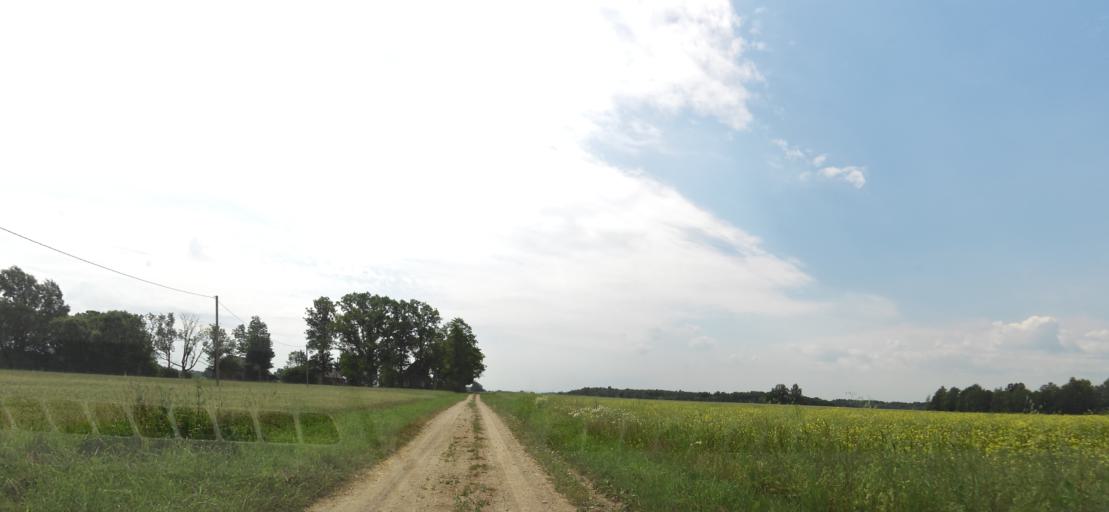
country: LT
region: Panevezys
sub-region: Birzai
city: Birzai
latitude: 56.3223
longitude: 24.7001
